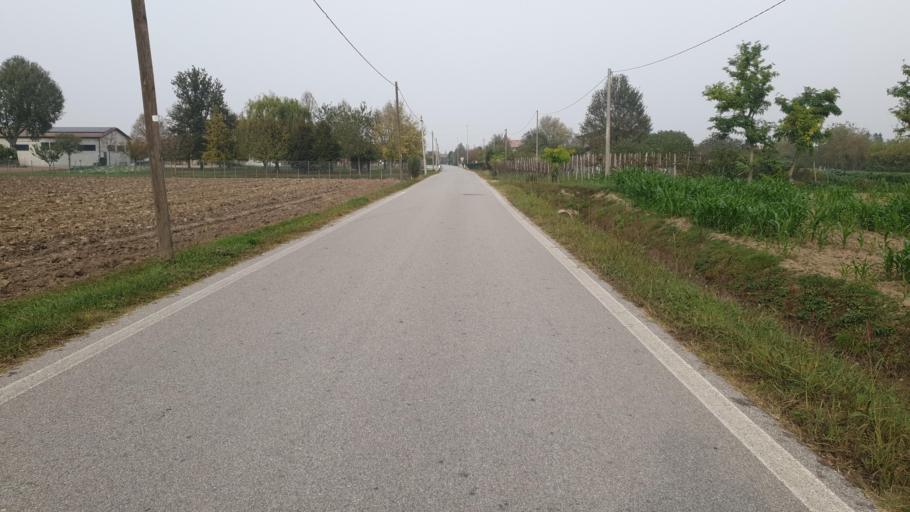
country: IT
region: Veneto
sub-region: Provincia di Padova
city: Casalserugo
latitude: 45.2895
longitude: 11.9073
